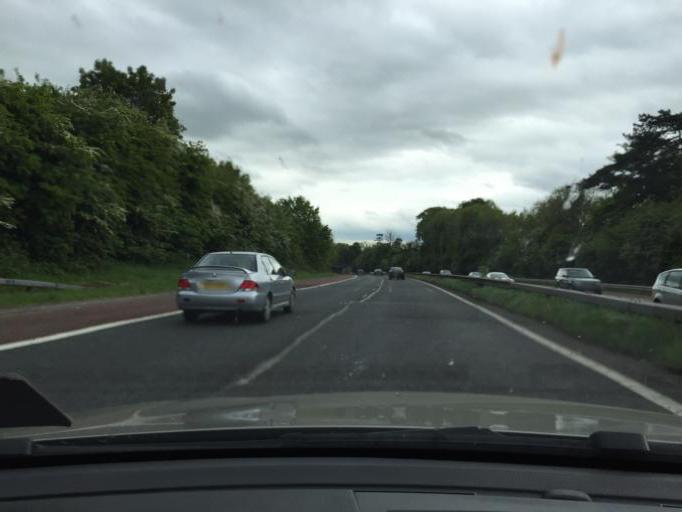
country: GB
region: Northern Ireland
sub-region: Lisburn District
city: Lisburn
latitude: 54.5547
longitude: -5.9964
